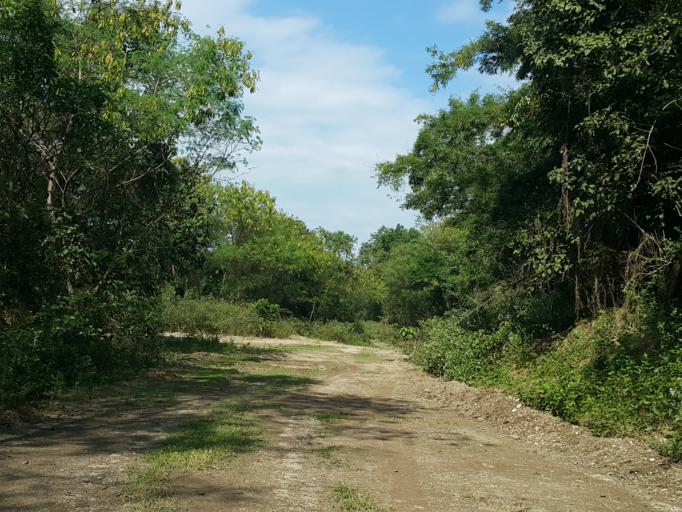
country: TH
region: Lampang
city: Mae Mo
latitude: 18.3322
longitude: 99.7669
